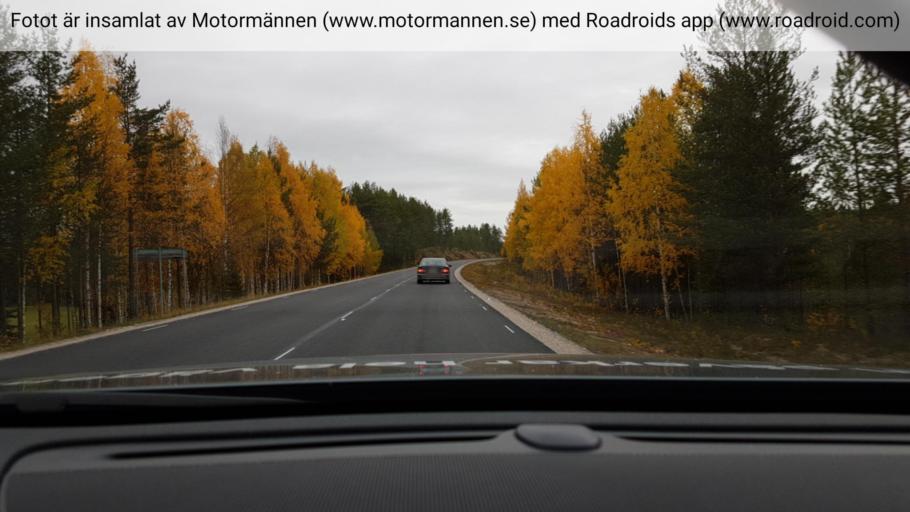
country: SE
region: Norrbotten
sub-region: Overkalix Kommun
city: OEverkalix
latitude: 66.4442
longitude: 22.7864
